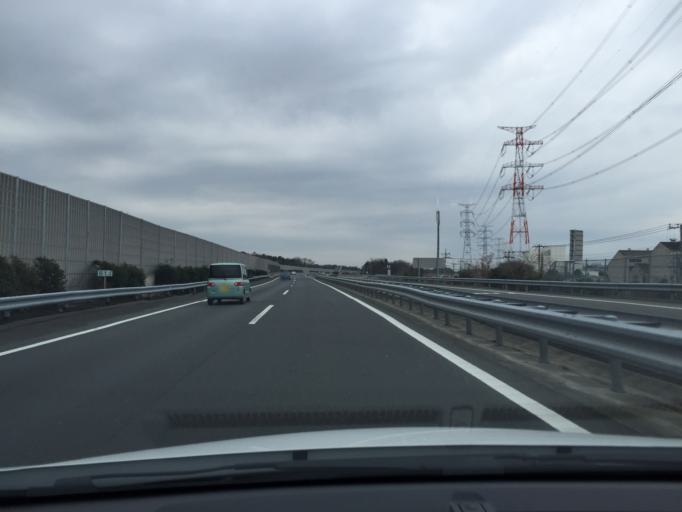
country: JP
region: Saitama
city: Sakado
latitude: 35.9554
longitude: 139.4291
